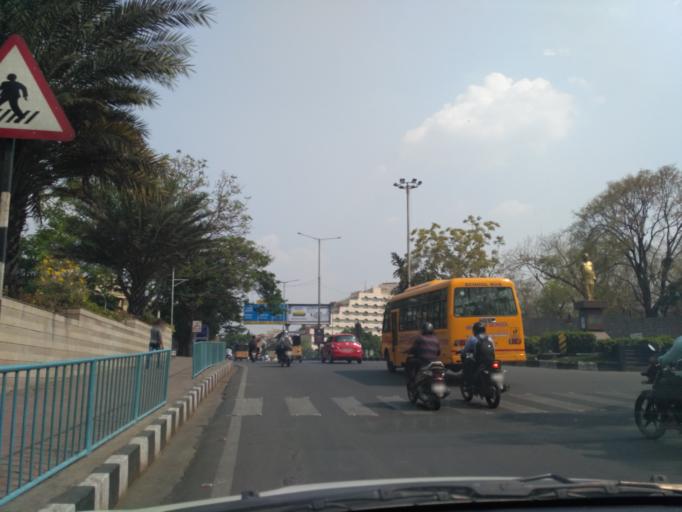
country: IN
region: Telangana
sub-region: Hyderabad
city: Hyderabad
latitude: 17.4187
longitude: 78.4484
